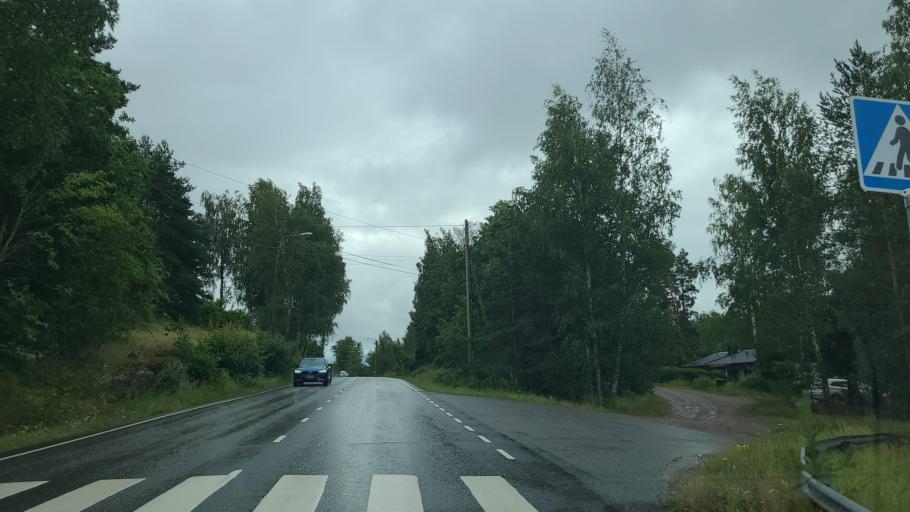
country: FI
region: Varsinais-Suomi
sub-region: Aboland-Turunmaa
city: Kimito
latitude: 60.1716
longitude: 22.7354
